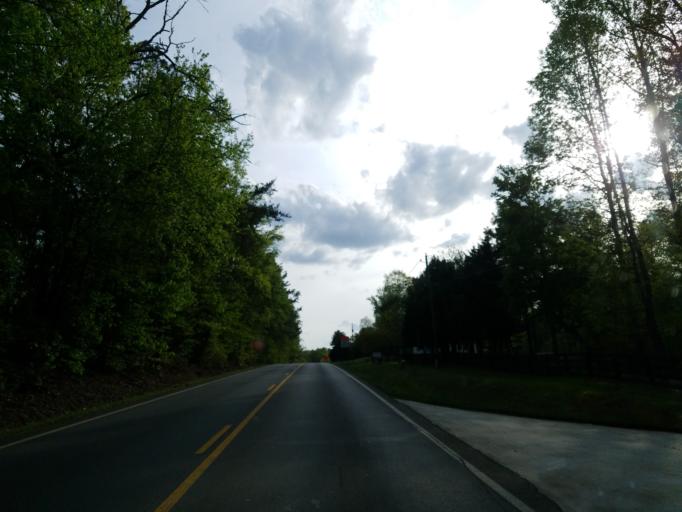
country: US
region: Georgia
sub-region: Cherokee County
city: Ball Ground
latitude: 34.2847
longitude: -84.2895
